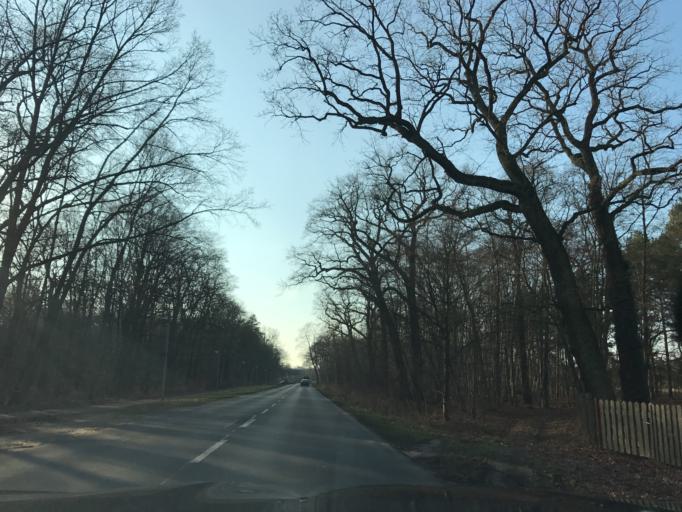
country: DE
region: Brandenburg
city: Brandenburg an der Havel
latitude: 52.3760
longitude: 12.5127
